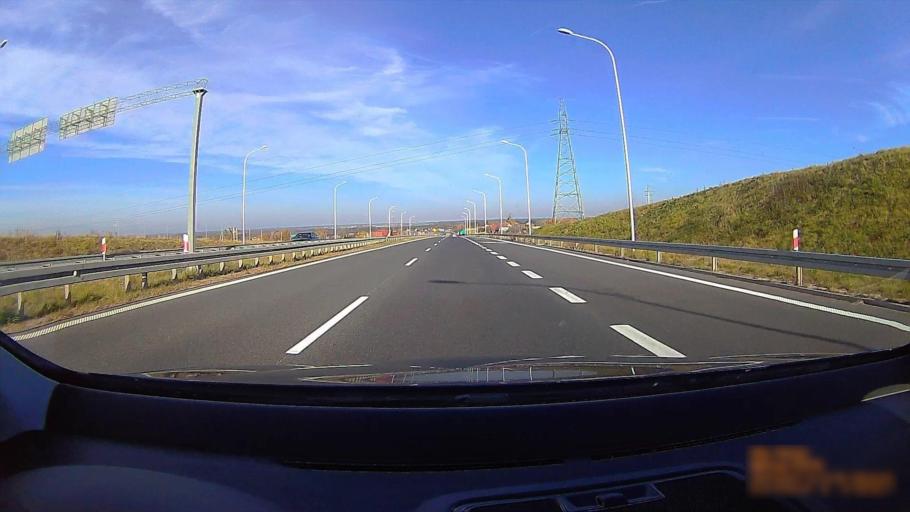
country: PL
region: Greater Poland Voivodeship
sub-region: Powiat ostrowski
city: Przygodzice
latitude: 51.6313
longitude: 17.8699
